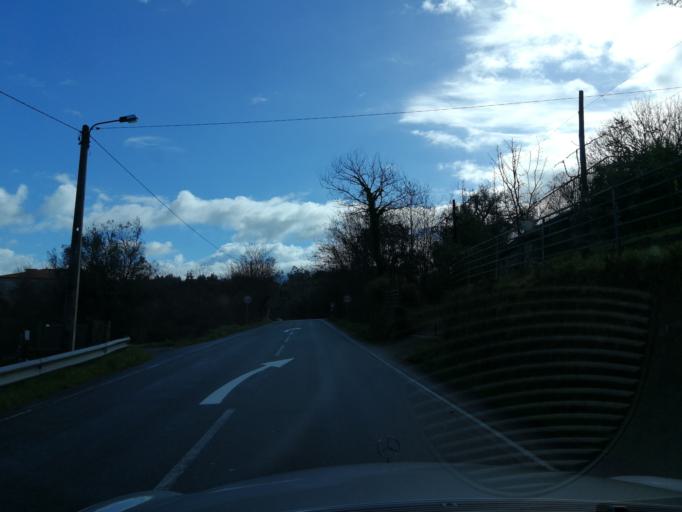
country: PT
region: Viana do Castelo
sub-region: Ponte da Barca
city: Ponte da Barca
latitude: 41.8100
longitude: -8.3598
